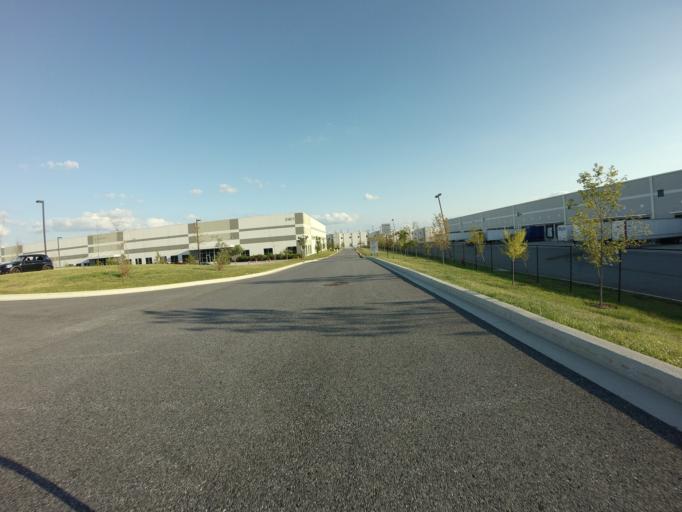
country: US
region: Maryland
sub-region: Baltimore County
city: Dundalk
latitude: 39.2708
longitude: -76.5466
